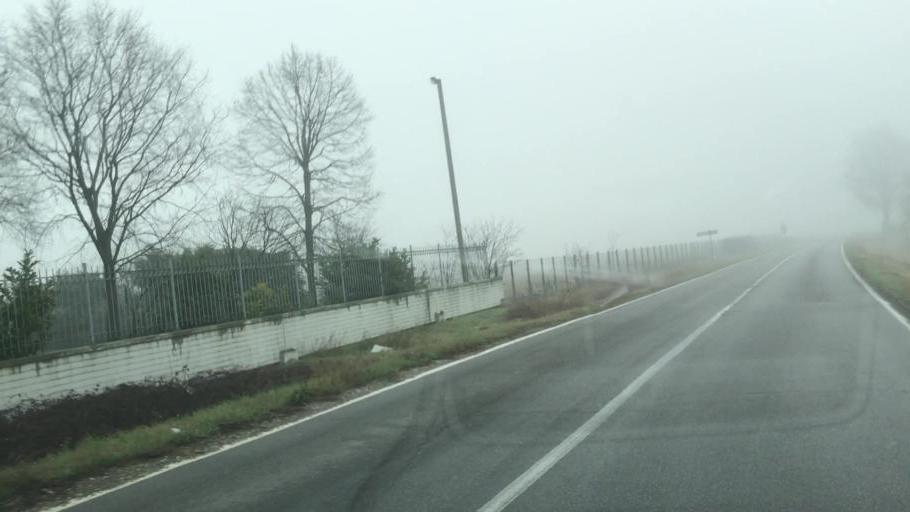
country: IT
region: Lombardy
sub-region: Provincia di Brescia
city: Montichiari
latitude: 45.3871
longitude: 10.4073
